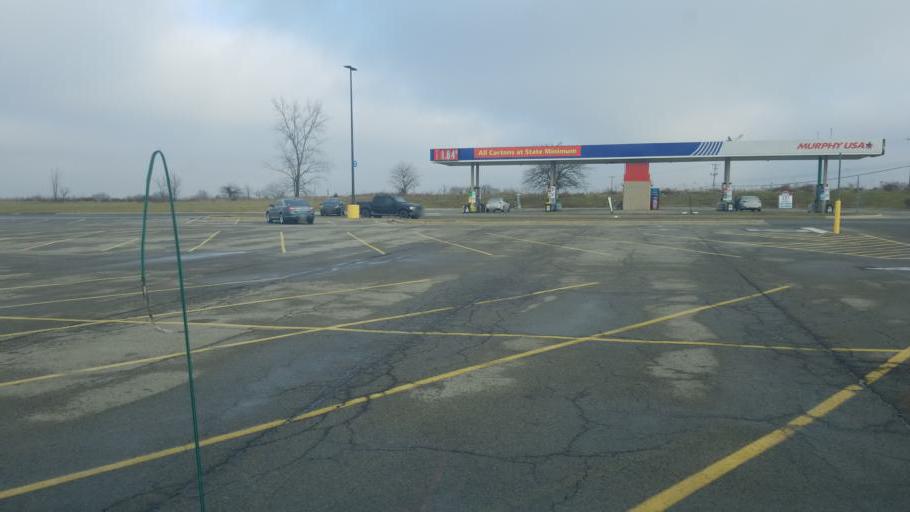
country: US
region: Ohio
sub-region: Hardin County
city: Kenton
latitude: 40.6559
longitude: -83.5833
